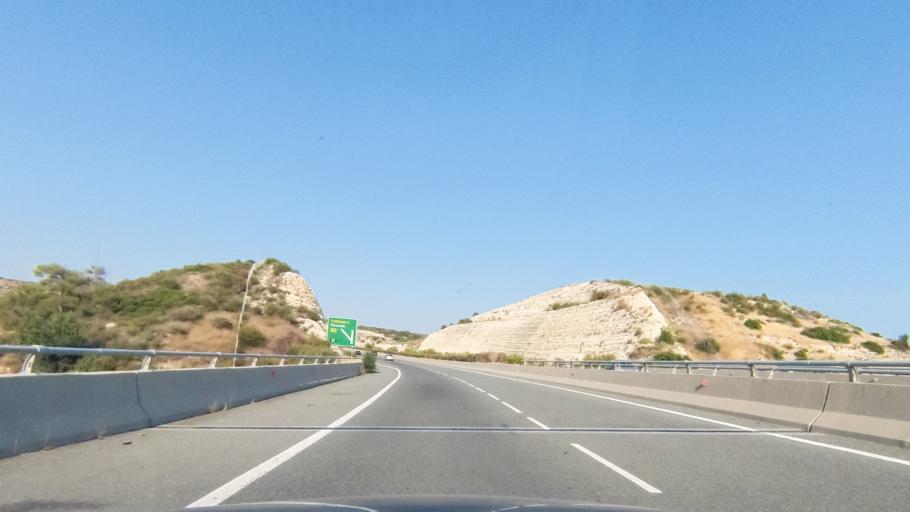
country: CY
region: Limassol
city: Sotira
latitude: 34.6783
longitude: 32.7968
